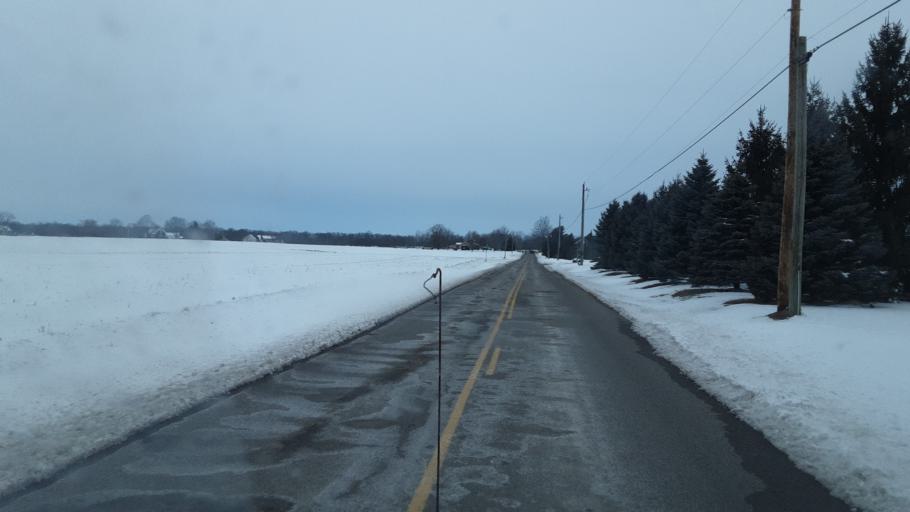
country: US
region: Ohio
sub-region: Madison County
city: Plain City
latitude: 40.1357
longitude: -83.2797
